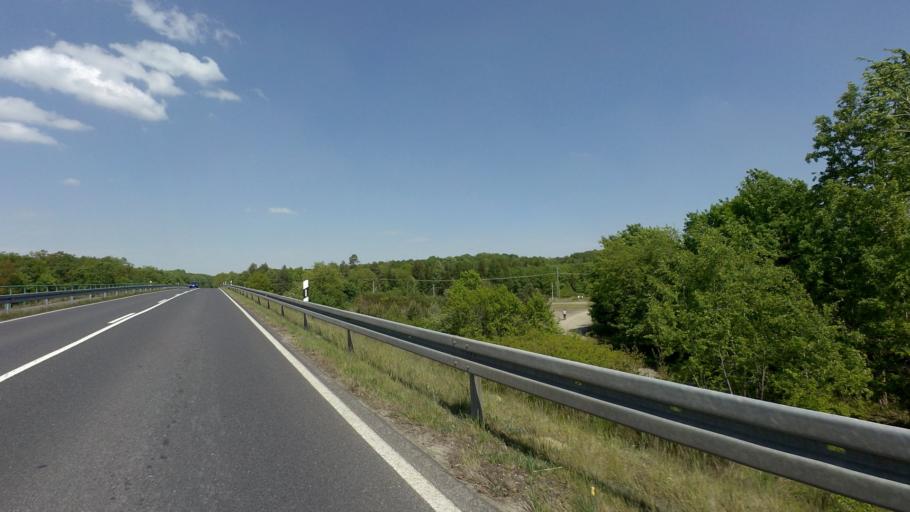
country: DE
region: Mecklenburg-Vorpommern
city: Neustrelitz
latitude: 53.4093
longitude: 13.0421
